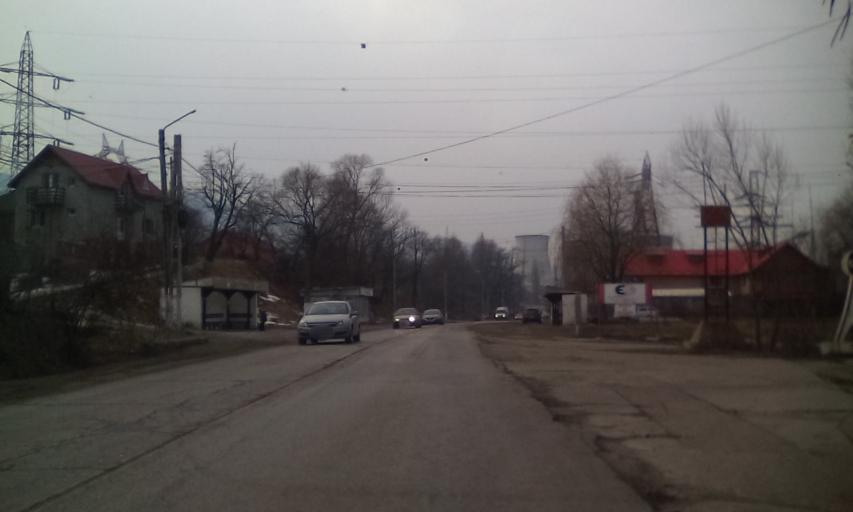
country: RO
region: Hunedoara
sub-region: Municipiul  Vulcan
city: Jiu-Paroseni
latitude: 45.3659
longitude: 23.2683
